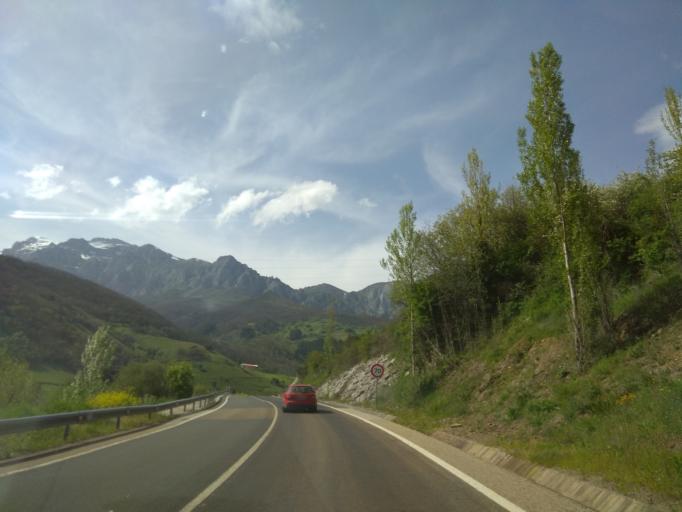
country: ES
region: Cantabria
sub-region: Provincia de Cantabria
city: Potes
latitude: 43.1855
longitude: -4.6027
